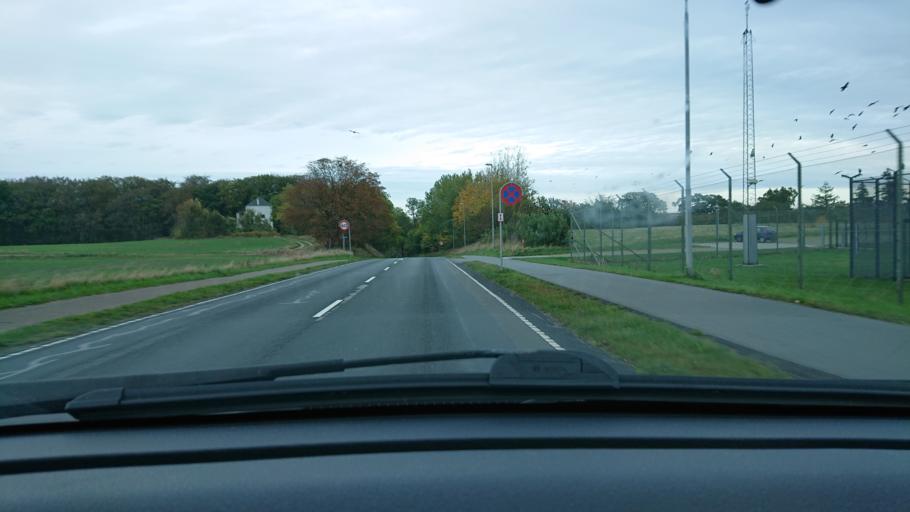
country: DK
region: South Denmark
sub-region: Nyborg Kommune
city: Nyborg
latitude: 55.3138
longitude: 10.7752
